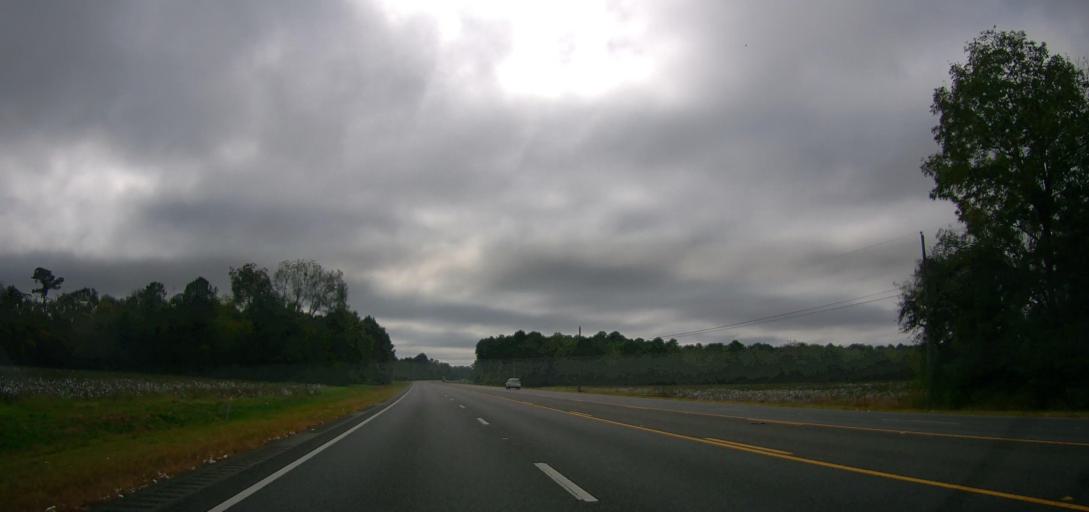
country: US
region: Georgia
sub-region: Colquitt County
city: Moultrie
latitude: 31.0659
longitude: -83.8267
